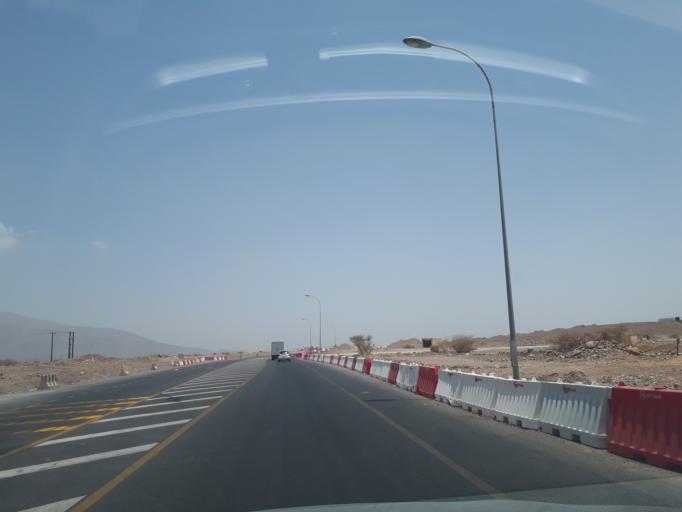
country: OM
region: Ash Sharqiyah
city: Badiyah
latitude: 22.4382
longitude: 59.0273
